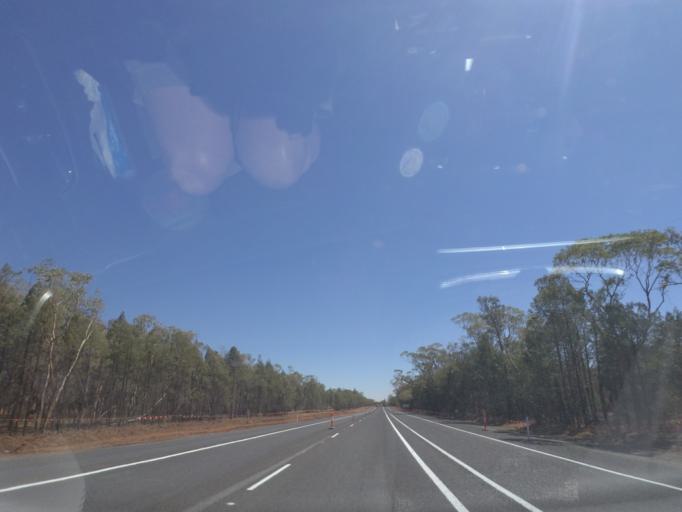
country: AU
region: New South Wales
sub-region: Gilgandra
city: Gilgandra
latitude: -31.6591
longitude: 148.7242
